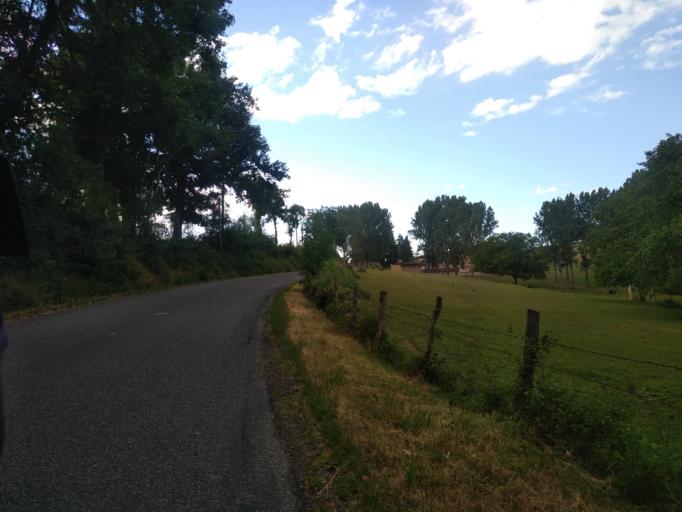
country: FR
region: Rhone-Alpes
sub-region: Departement de la Loire
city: Panissieres
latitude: 45.7436
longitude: 4.3496
